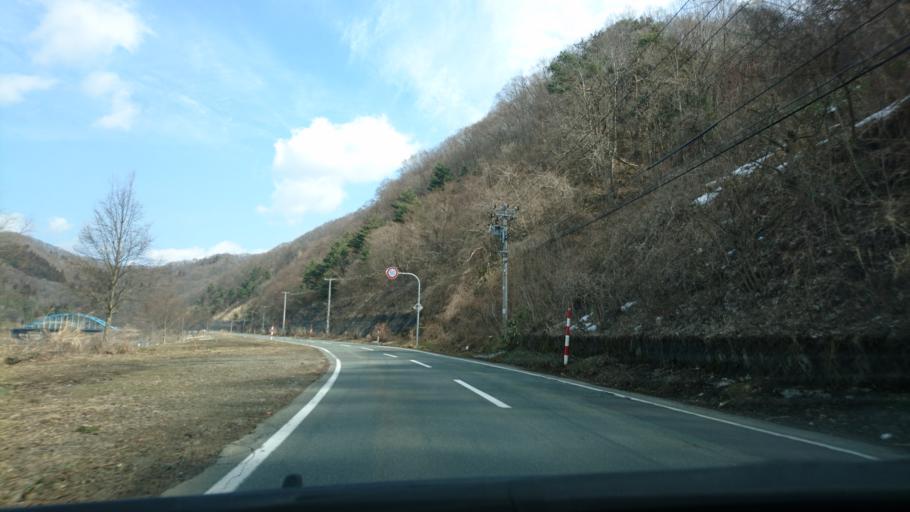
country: JP
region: Iwate
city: Shizukuishi
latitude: 39.6834
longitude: 141.0293
